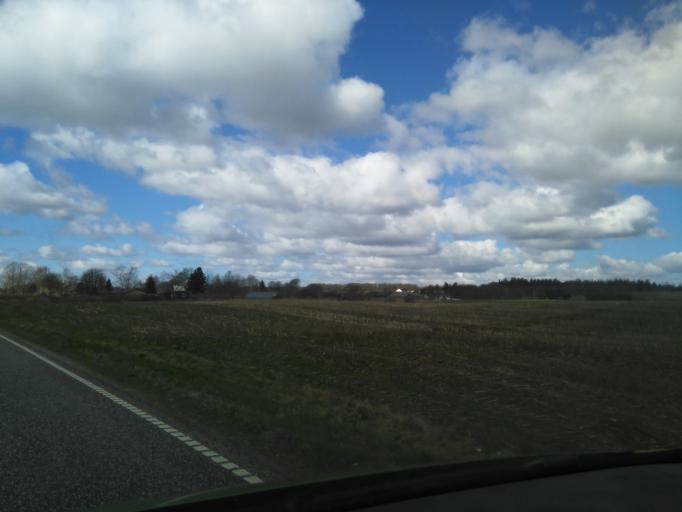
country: DK
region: Central Jutland
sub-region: Horsens Kommune
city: Braedstrup
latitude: 56.0289
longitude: 9.5204
